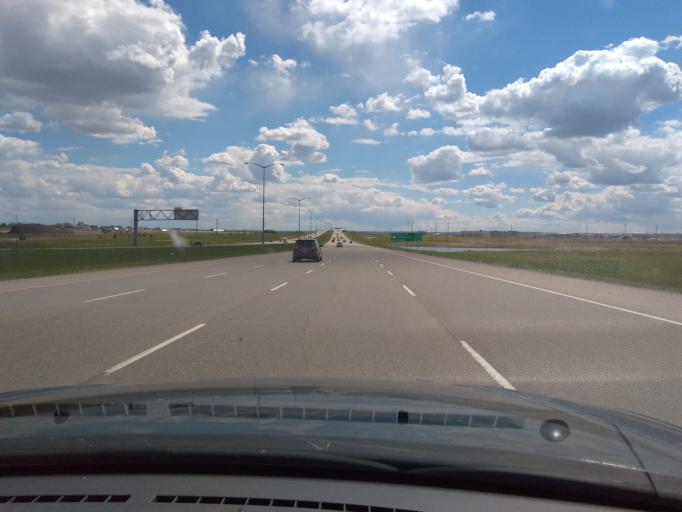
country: CA
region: Alberta
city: Chestermere
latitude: 50.9671
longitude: -113.9212
